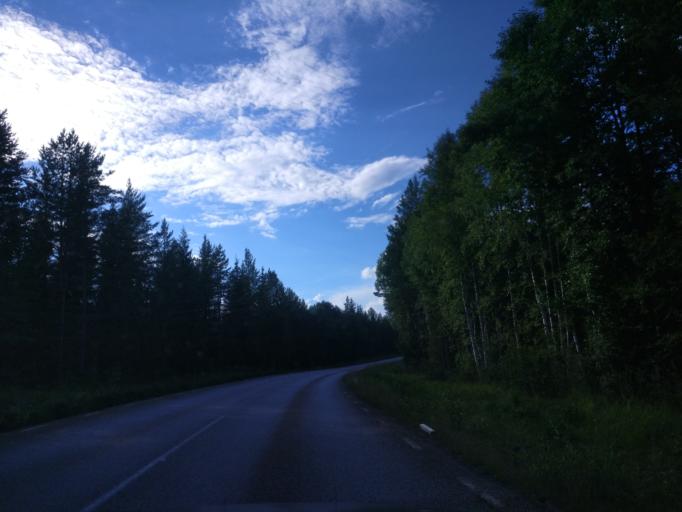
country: SE
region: Dalarna
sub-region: Ludvika Kommun
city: Ludvika
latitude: 60.2860
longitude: 15.1423
